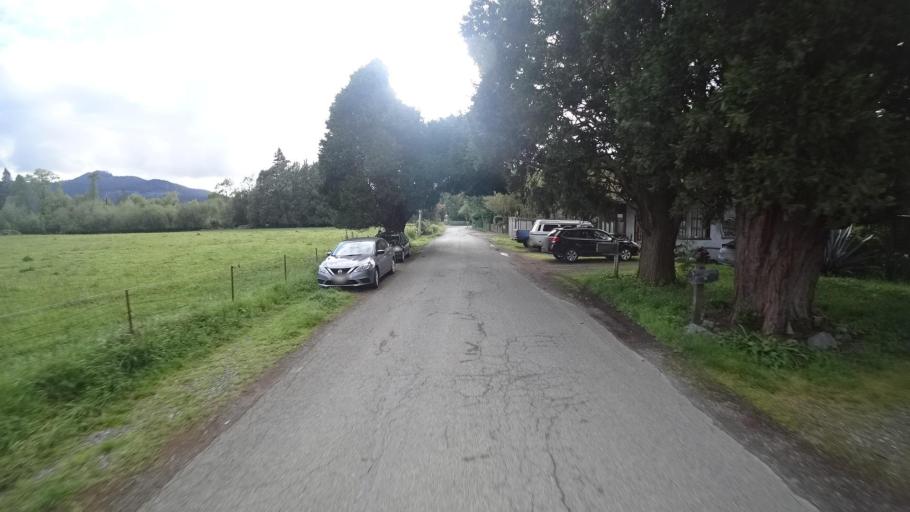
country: US
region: California
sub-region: Humboldt County
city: Blue Lake
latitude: 40.8682
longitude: -123.9973
